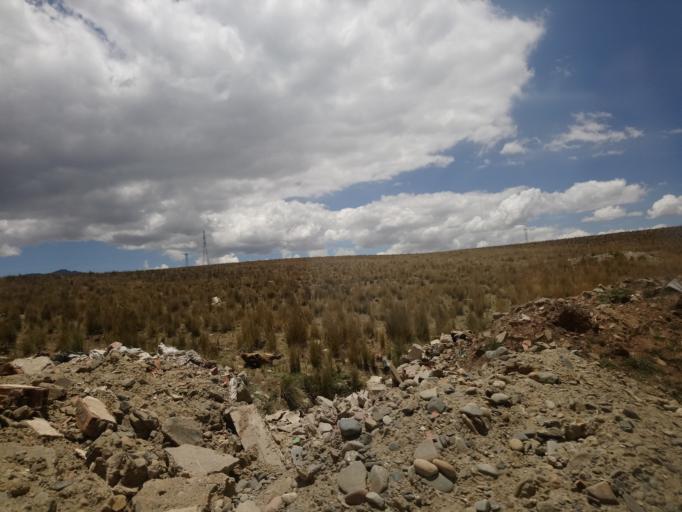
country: BO
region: La Paz
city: La Paz
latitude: -16.4373
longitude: -68.1628
